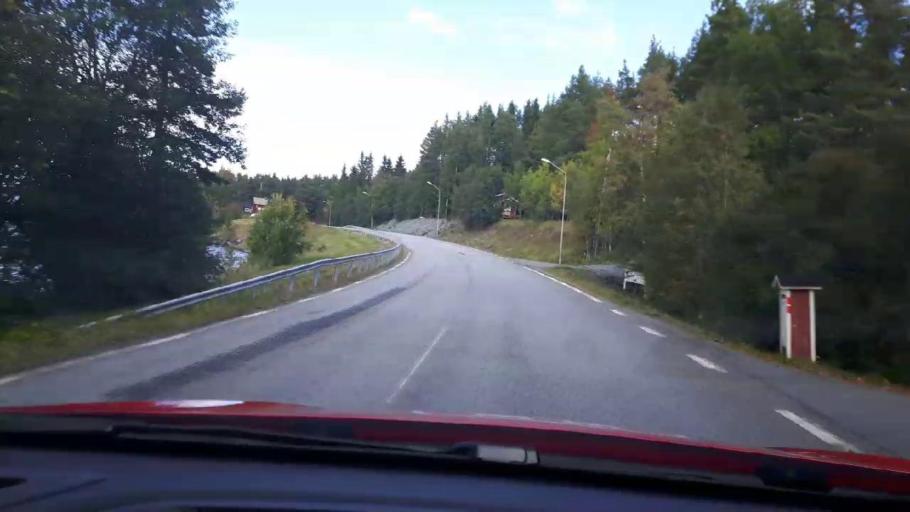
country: SE
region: Jaemtland
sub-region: Bergs Kommun
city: Hoverberg
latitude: 62.9849
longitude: 14.4820
